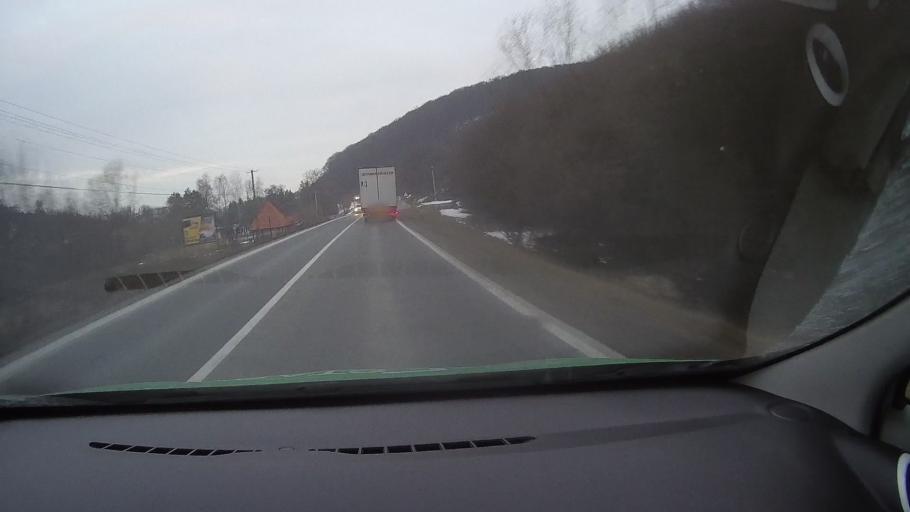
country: RO
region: Harghita
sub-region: Municipiul Odorheiu Secuiesc
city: Odorheiu Secuiesc
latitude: 46.3348
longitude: 25.2710
